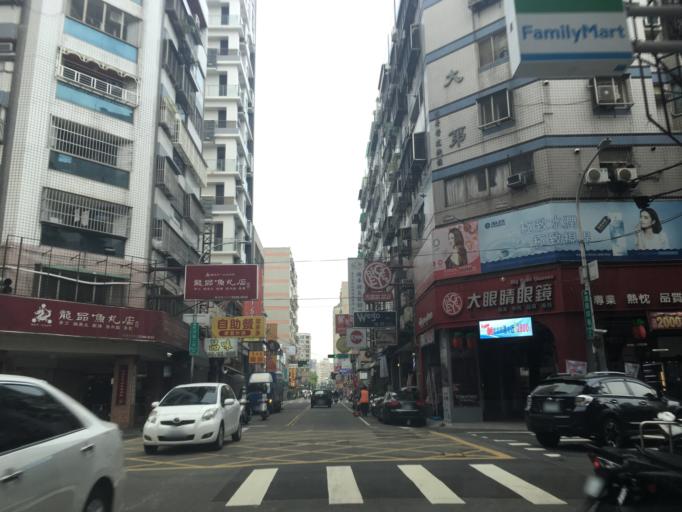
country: TW
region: Taiwan
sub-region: Taichung City
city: Taichung
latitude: 24.1723
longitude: 120.6877
